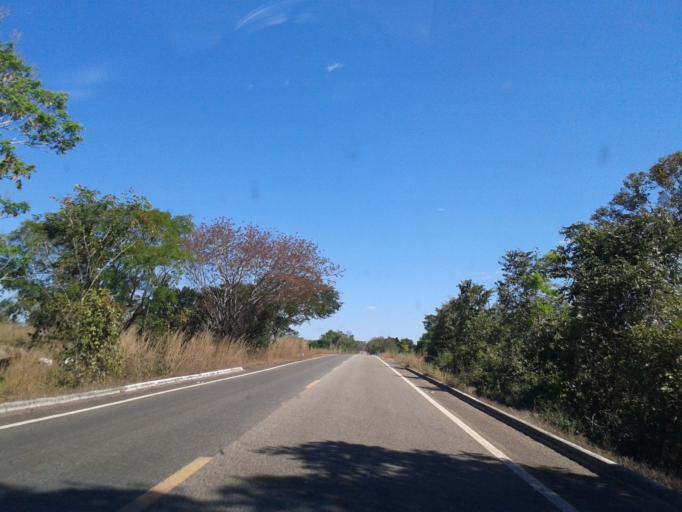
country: BR
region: Goias
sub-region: Sao Miguel Do Araguaia
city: Sao Miguel do Araguaia
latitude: -13.6674
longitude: -50.3264
